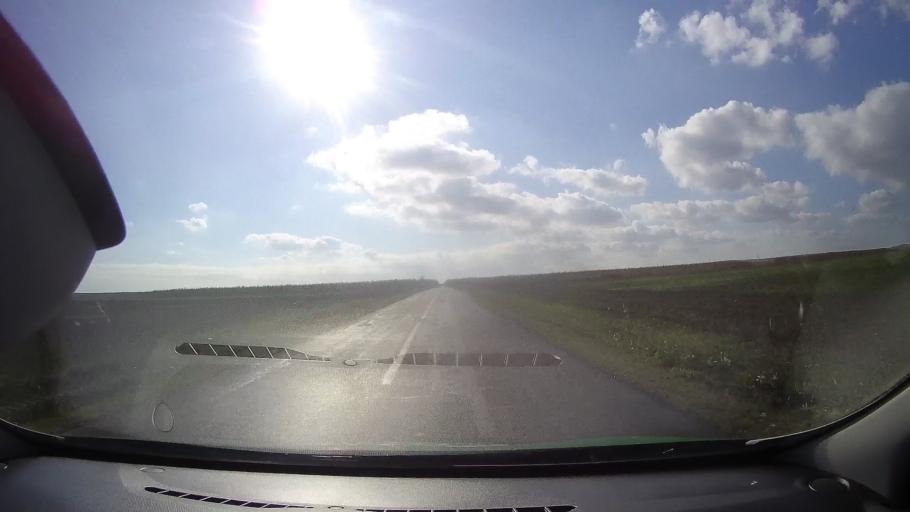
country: RO
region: Constanta
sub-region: Comuna Mihai Viteazu
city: Mihai Viteazu
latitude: 44.6184
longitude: 28.7264
